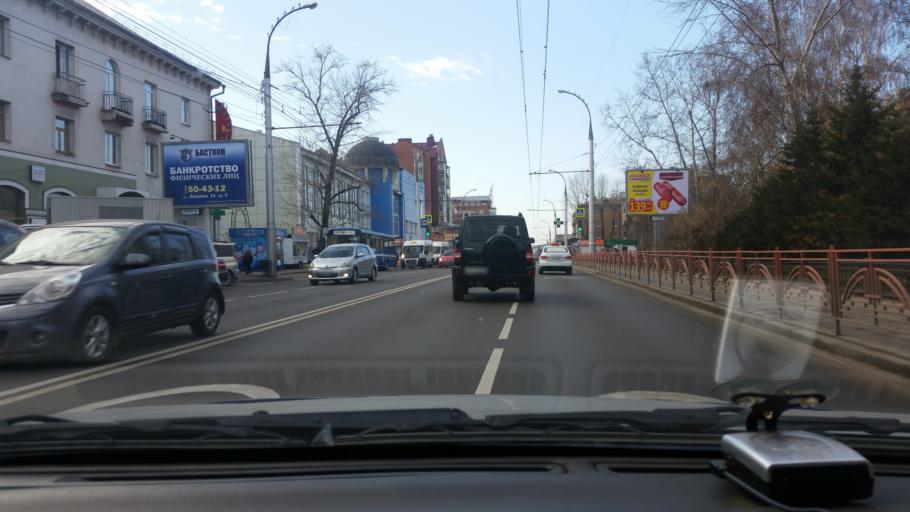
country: RU
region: Irkutsk
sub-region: Irkutskiy Rayon
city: Irkutsk
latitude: 52.2799
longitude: 104.3354
